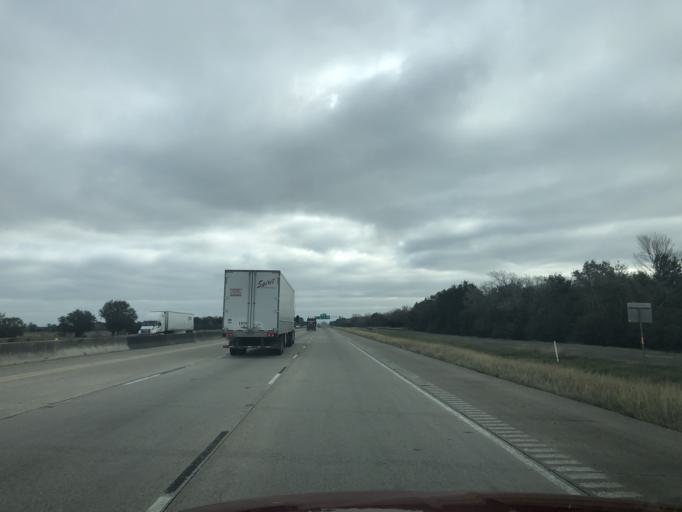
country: US
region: Texas
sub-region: Chambers County
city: Winnie
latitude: 29.8269
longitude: -94.4279
